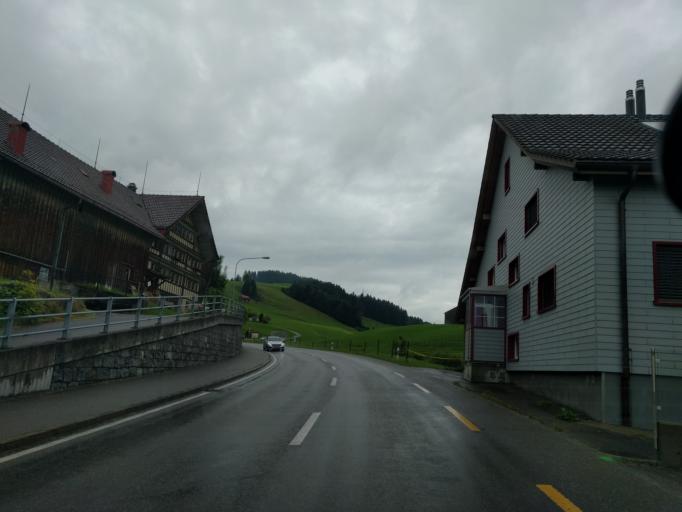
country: CH
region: Appenzell Ausserrhoden
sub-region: Bezirk Hinterland
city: Schwellbrunn
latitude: 47.3345
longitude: 9.2356
